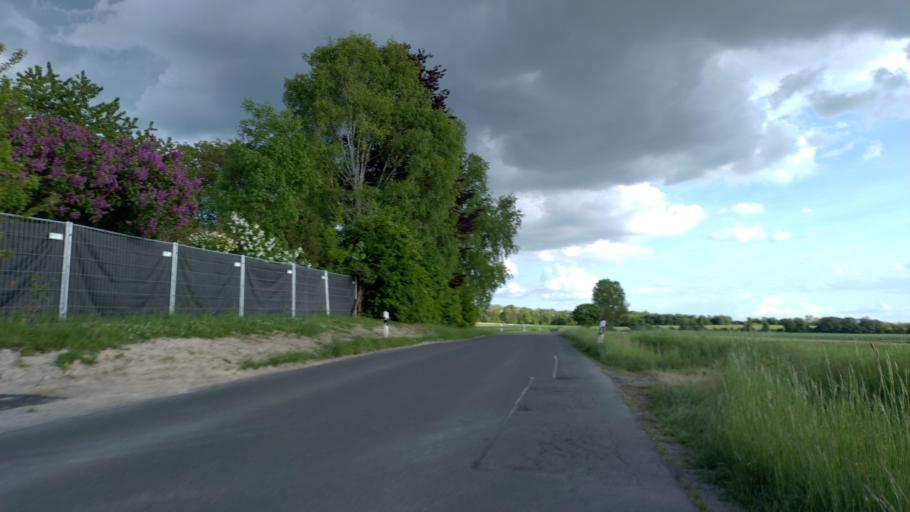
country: DE
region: Bavaria
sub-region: Upper Franconia
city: Bindlach
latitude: 49.9764
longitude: 11.6261
